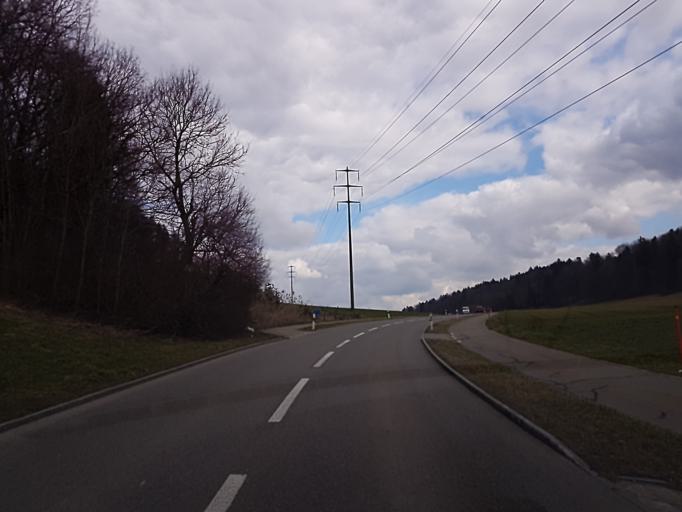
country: CH
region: Zurich
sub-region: Bezirk Dietikon
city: Unterengstringen
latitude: 47.4256
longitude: 8.4469
